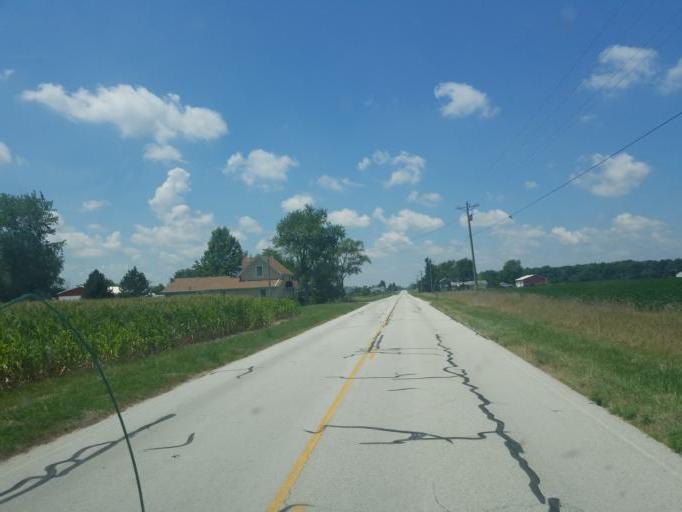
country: US
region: Ohio
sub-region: Allen County
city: Spencerville
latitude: 40.6773
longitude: -84.4615
